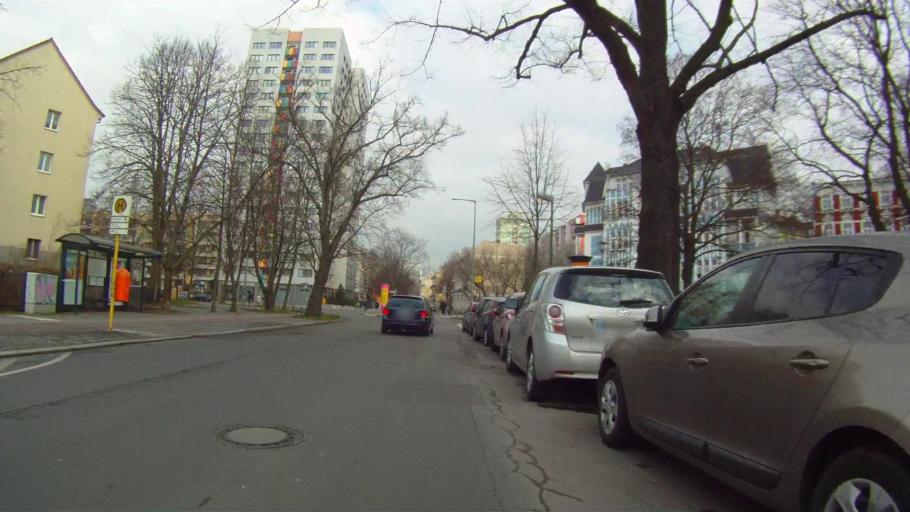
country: DE
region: Berlin
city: Friedrichsfelde
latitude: 52.5065
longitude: 13.5118
